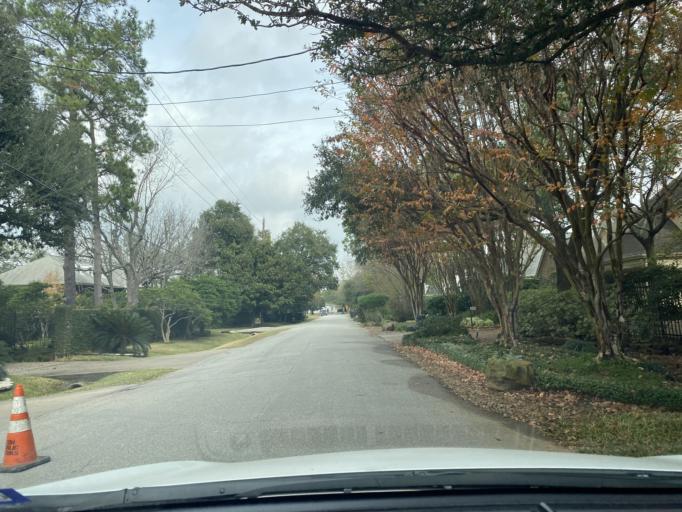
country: US
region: Texas
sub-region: Harris County
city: Hunters Creek Village
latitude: 29.7643
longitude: -95.4748
